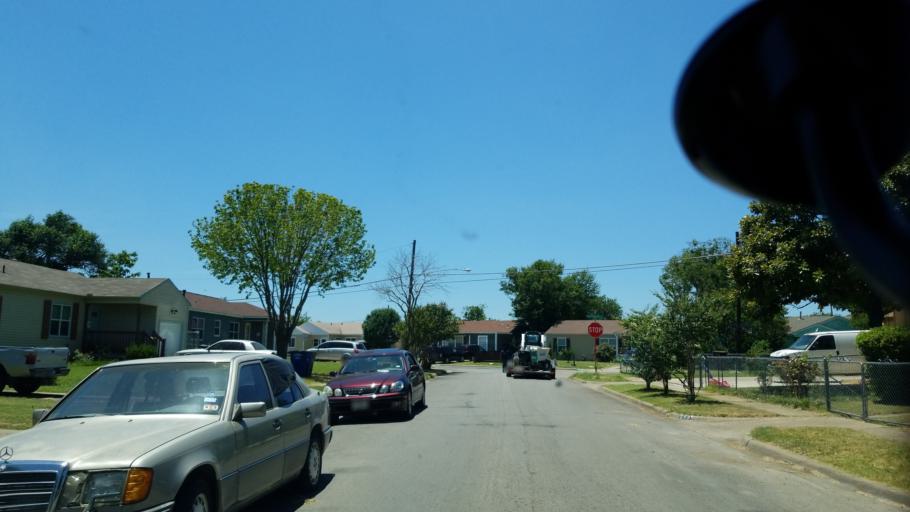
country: US
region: Texas
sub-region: Dallas County
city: Cockrell Hill
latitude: 32.7080
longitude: -96.8348
